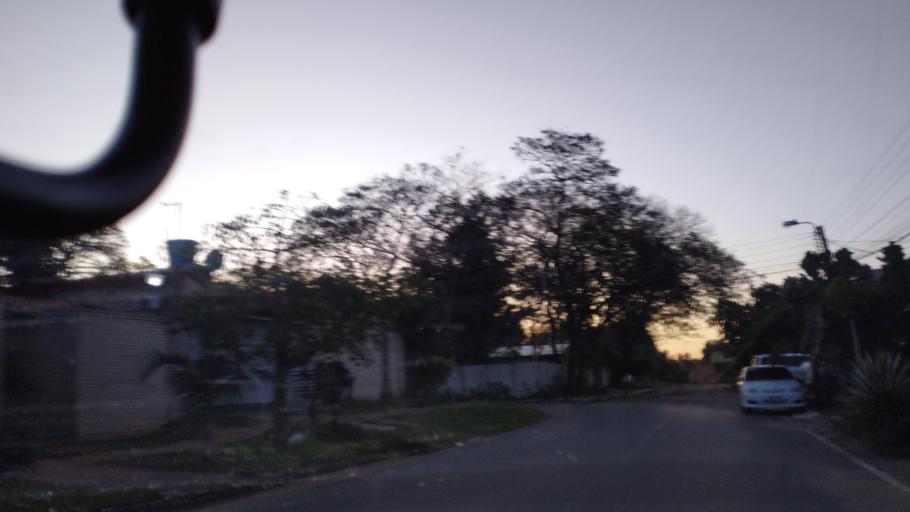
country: PY
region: Central
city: Fernando de la Mora
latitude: -25.3017
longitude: -57.5159
